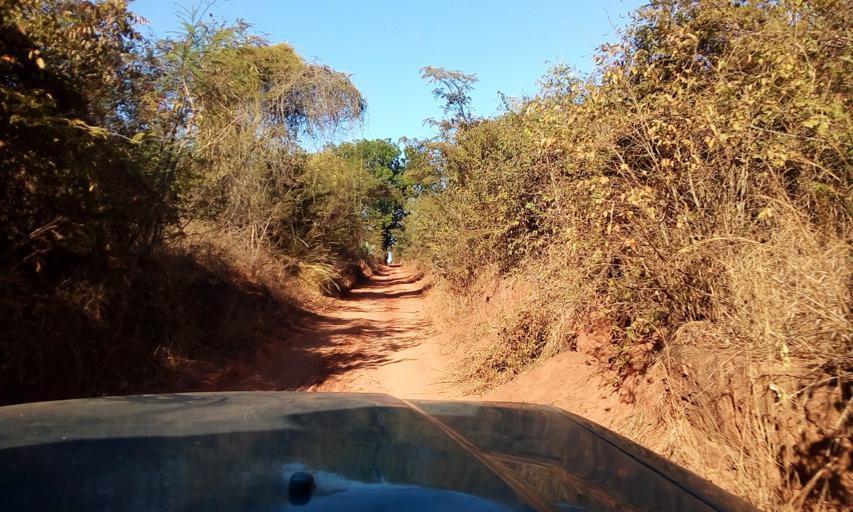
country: MG
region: Boeny
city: Sitampiky
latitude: -16.1928
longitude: 45.3613
